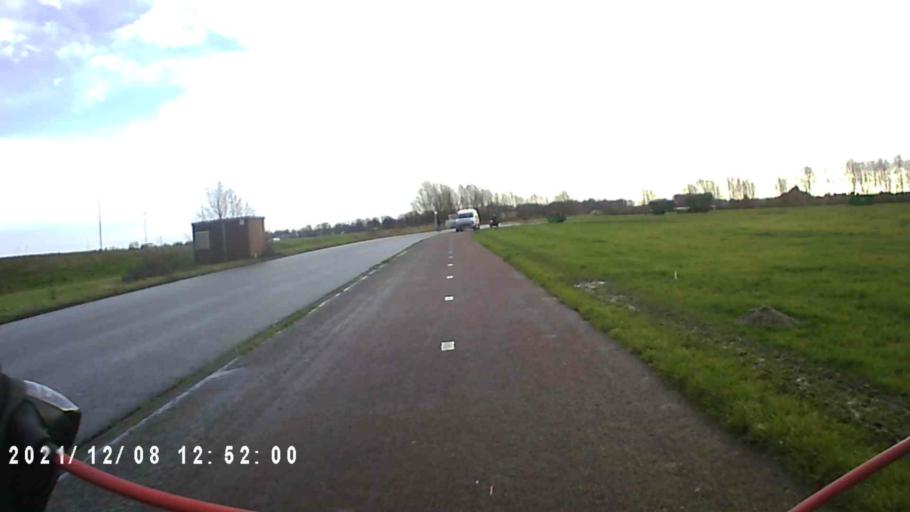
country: NL
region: Groningen
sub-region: Gemeente Haren
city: Haren
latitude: 53.2034
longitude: 6.6293
